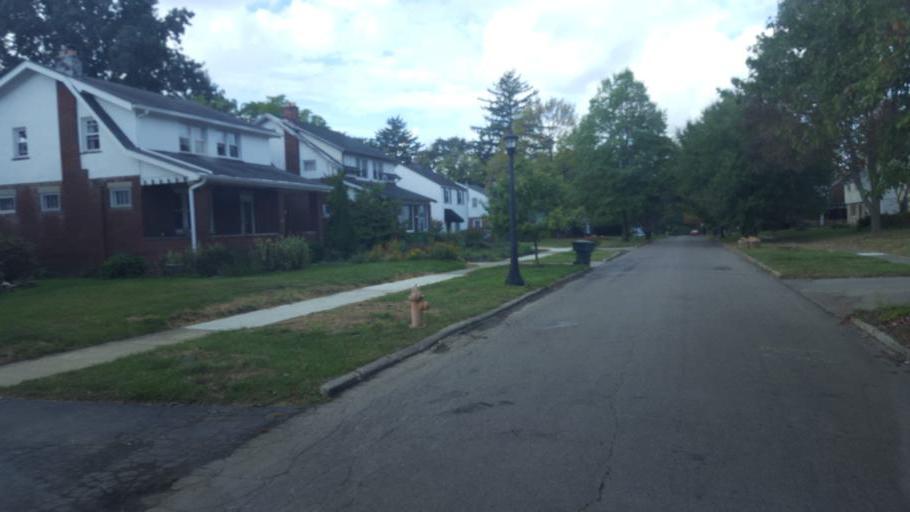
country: US
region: Ohio
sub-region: Franklin County
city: Worthington
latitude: 40.0434
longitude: -83.0083
